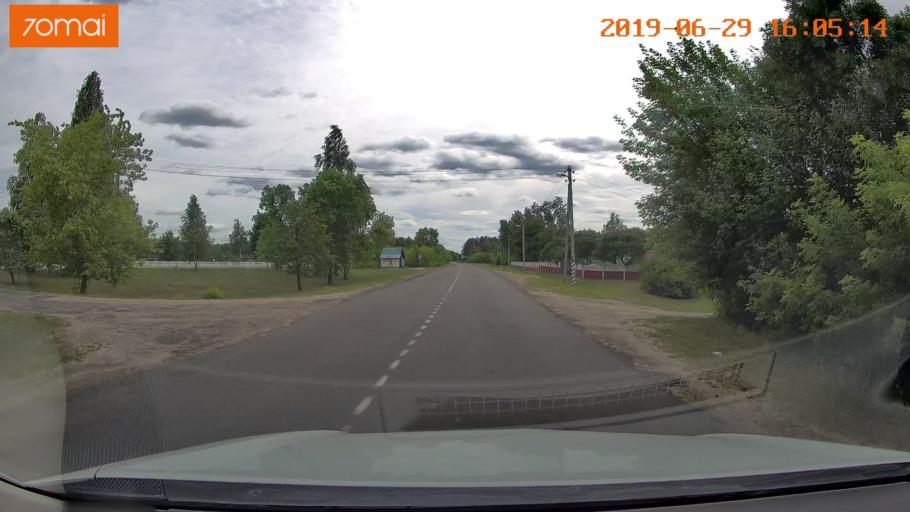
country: BY
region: Brest
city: Luninyets
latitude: 52.2176
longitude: 27.0204
